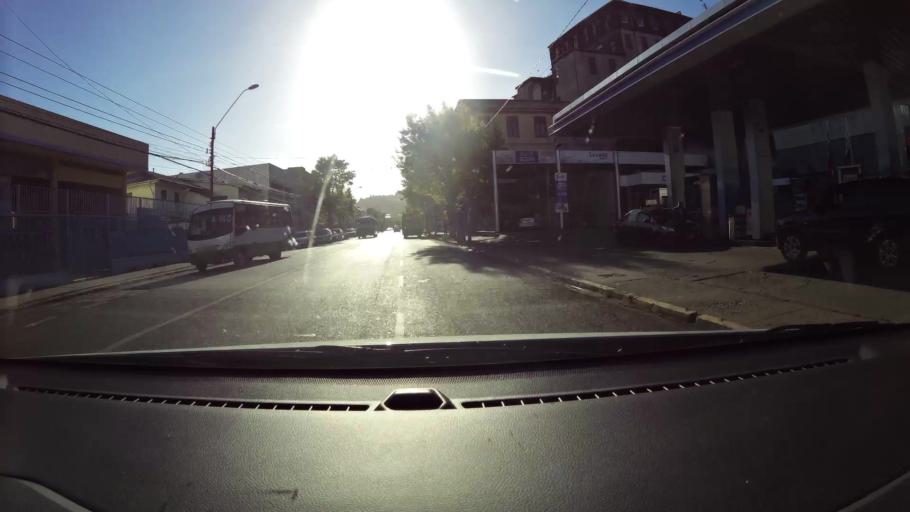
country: CL
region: Valparaiso
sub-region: Provincia de Valparaiso
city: Valparaiso
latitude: -33.0498
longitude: -71.6125
